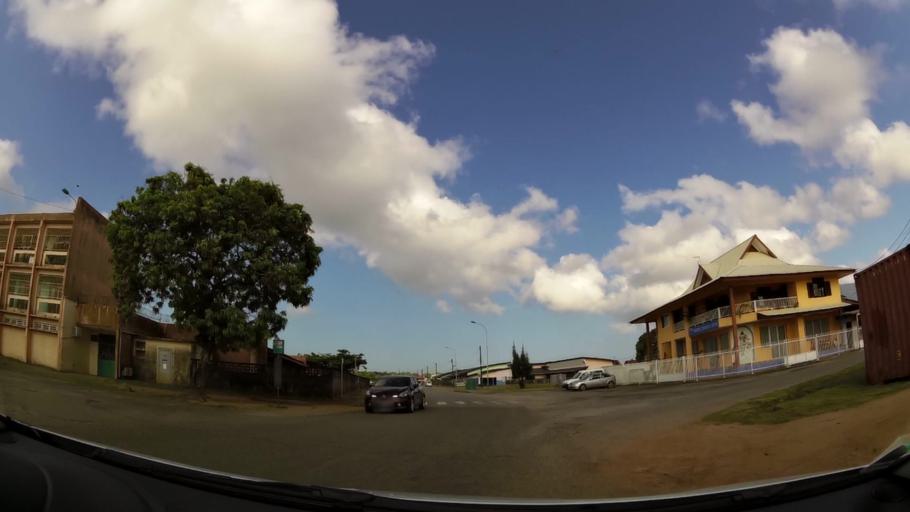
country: GF
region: Guyane
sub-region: Guyane
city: Cayenne
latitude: 4.9313
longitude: -52.3205
